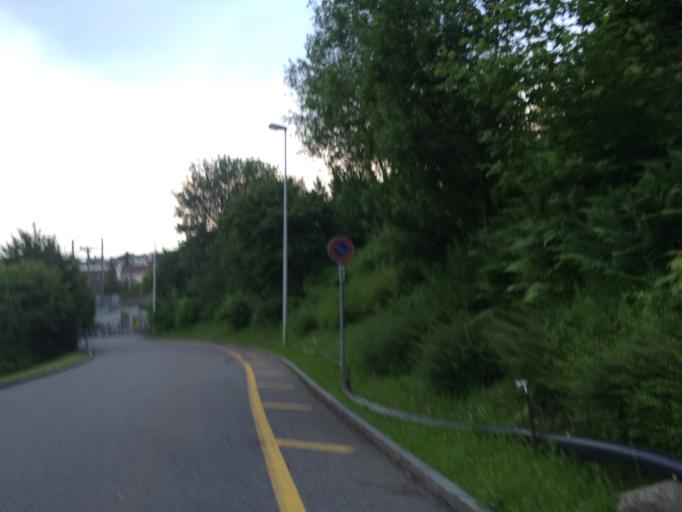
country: CH
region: Zurich
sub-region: Bezirk Horgen
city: Horgen / Oberdorf
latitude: 47.2579
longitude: 8.5897
